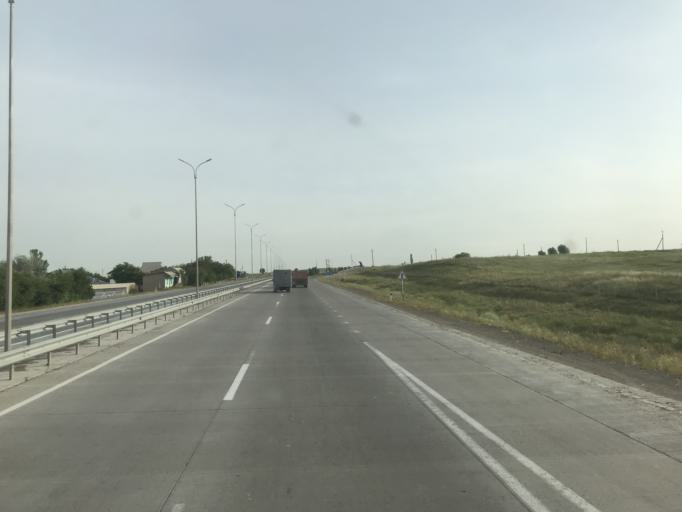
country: UZ
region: Toshkent
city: Qibray
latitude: 41.5631
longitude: 69.4084
